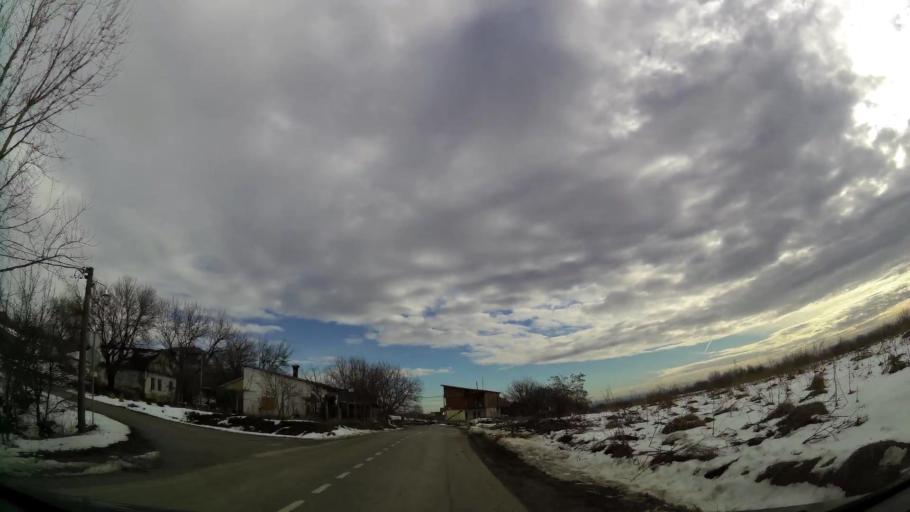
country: RS
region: Central Serbia
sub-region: Belgrade
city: Surcin
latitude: 44.7893
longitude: 20.2802
